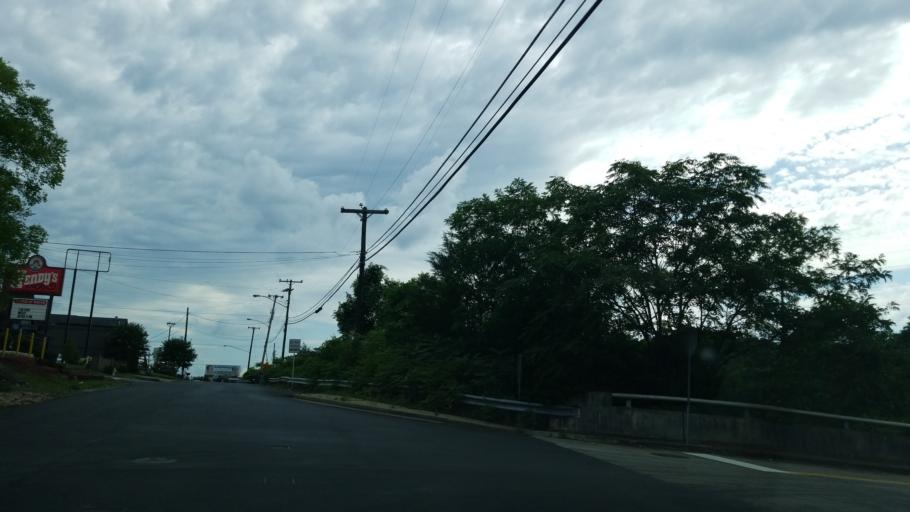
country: US
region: Tennessee
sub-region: Williamson County
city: Brentwood
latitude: 36.0391
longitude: -86.7850
